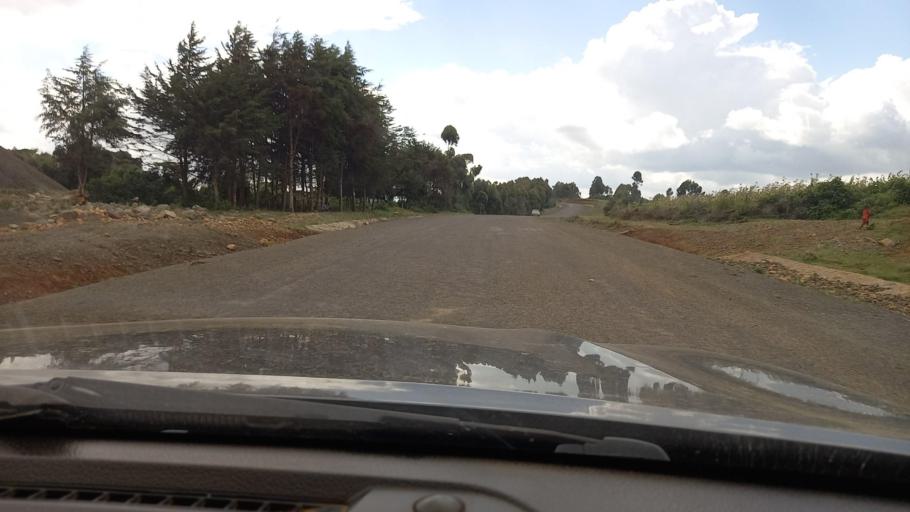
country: ET
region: Southern Nations, Nationalities, and People's Region
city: Mizan Teferi
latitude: 6.2145
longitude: 35.6257
